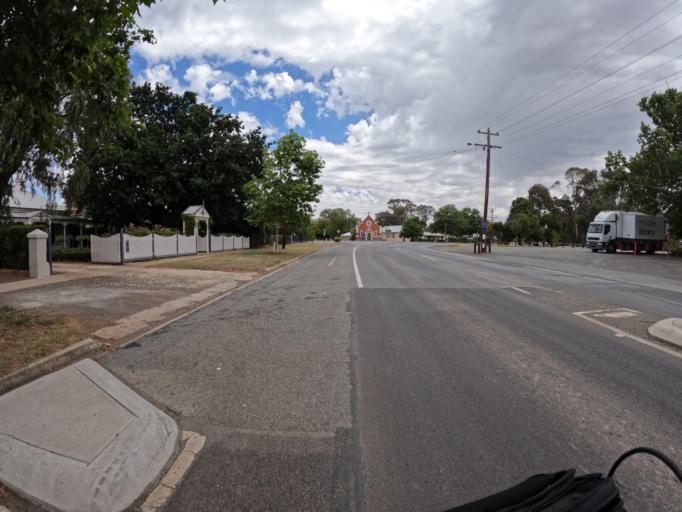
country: AU
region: Victoria
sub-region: Greater Shepparton
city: Shepparton
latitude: -36.6163
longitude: 145.2165
